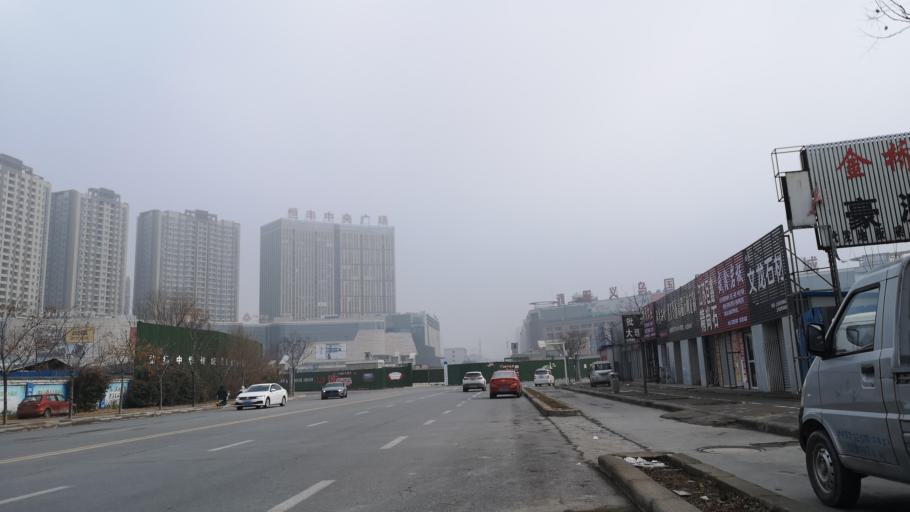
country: CN
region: Henan Sheng
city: Zhongyuanlu
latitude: 35.7757
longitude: 115.0518
